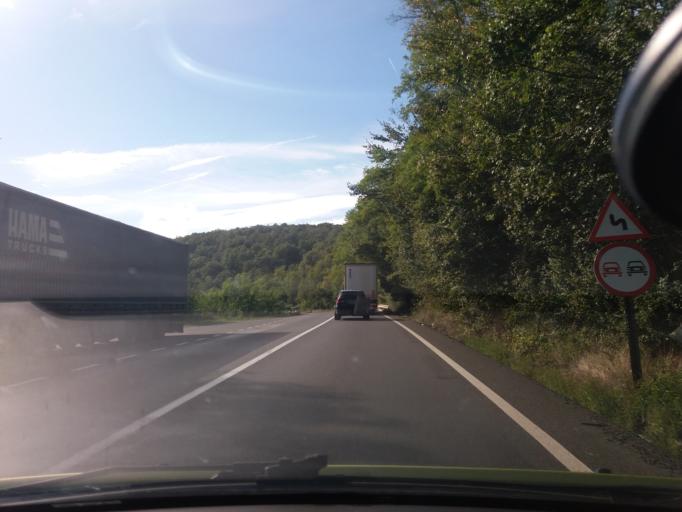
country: RO
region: Arad
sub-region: Comuna Bata
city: Bata
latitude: 46.0370
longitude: 22.0794
